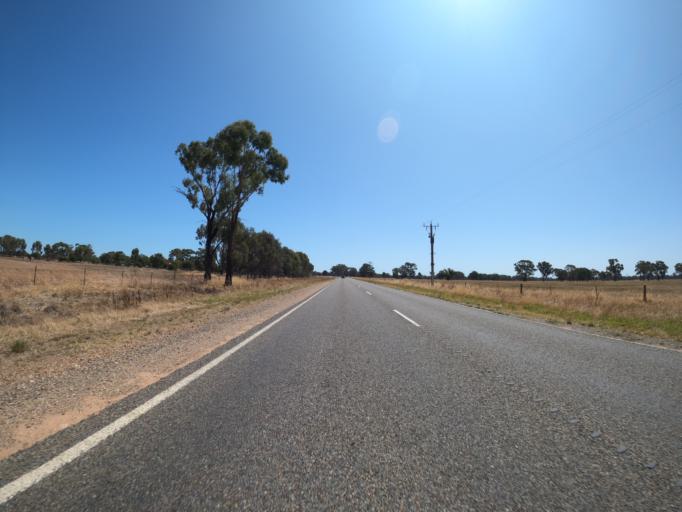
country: AU
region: New South Wales
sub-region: Corowa Shire
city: Corowa
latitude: -36.0661
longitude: 146.3672
